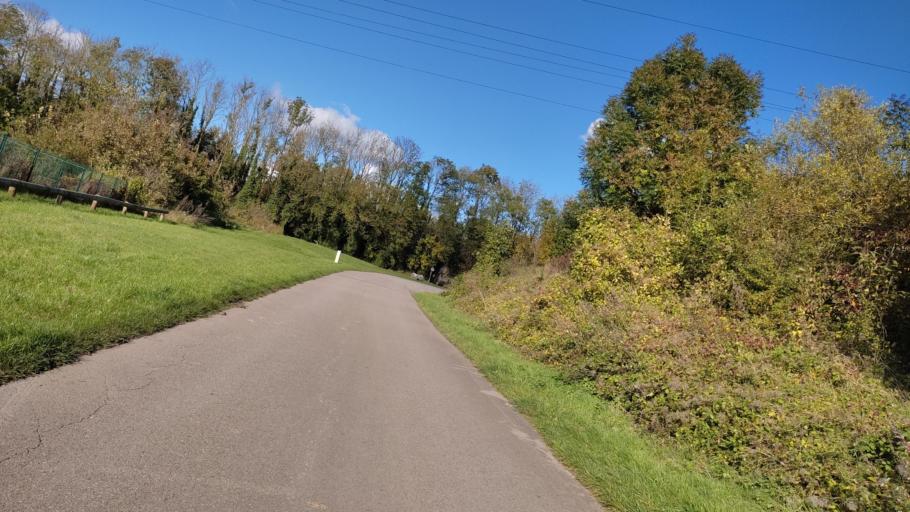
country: FR
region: Nord-Pas-de-Calais
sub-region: Departement du Pas-de-Calais
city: Saint-Laurent-Blangy
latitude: 50.3069
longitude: 2.8205
